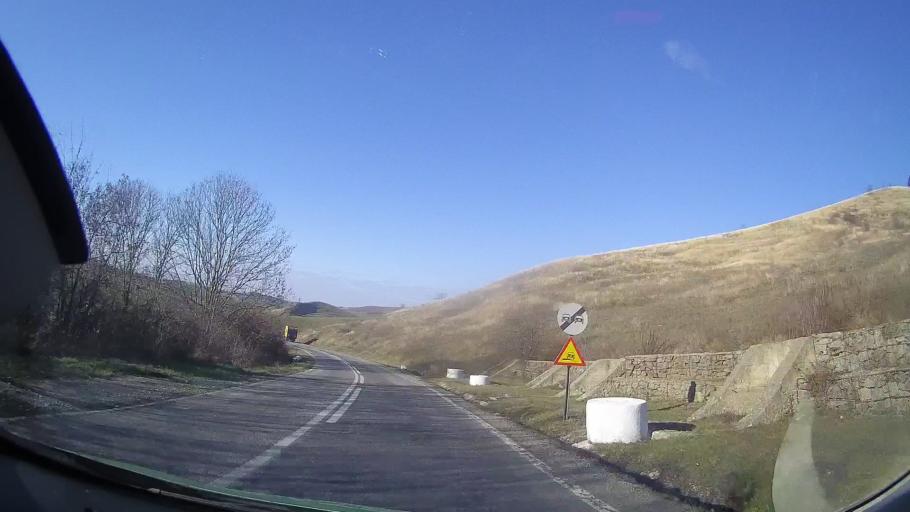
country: RO
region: Mures
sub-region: Comuna Sarmasu
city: Sarmasu
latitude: 46.7945
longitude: 24.1836
